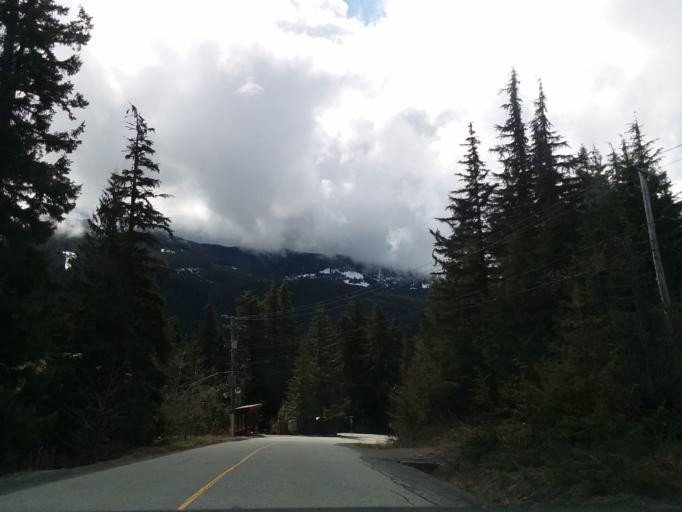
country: CA
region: British Columbia
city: Whistler
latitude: 50.0974
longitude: -123.0021
